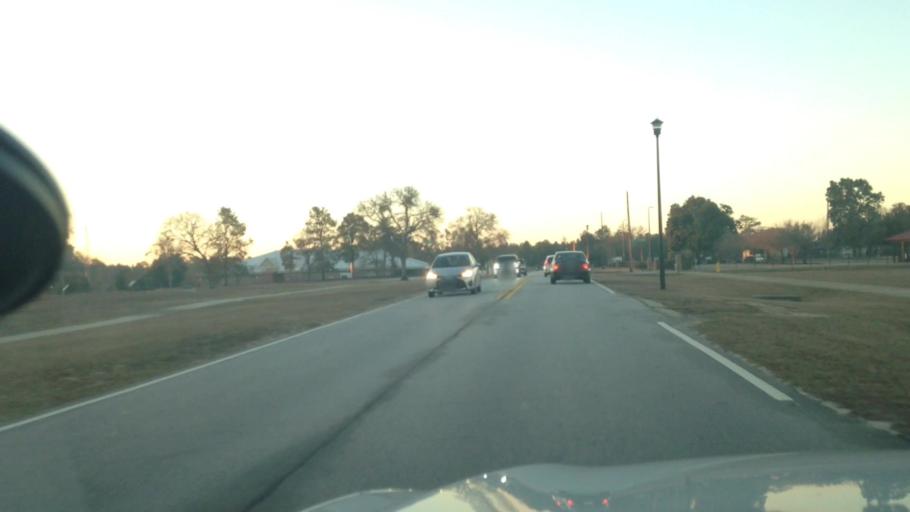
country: US
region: Georgia
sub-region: Columbia County
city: Grovetown
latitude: 33.4220
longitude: -82.1354
